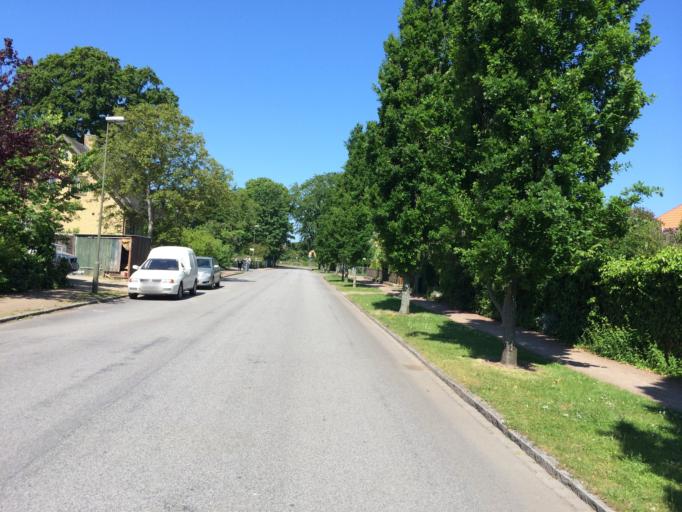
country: SE
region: Skane
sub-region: Malmo
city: Bunkeflostrand
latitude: 55.5784
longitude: 12.9418
